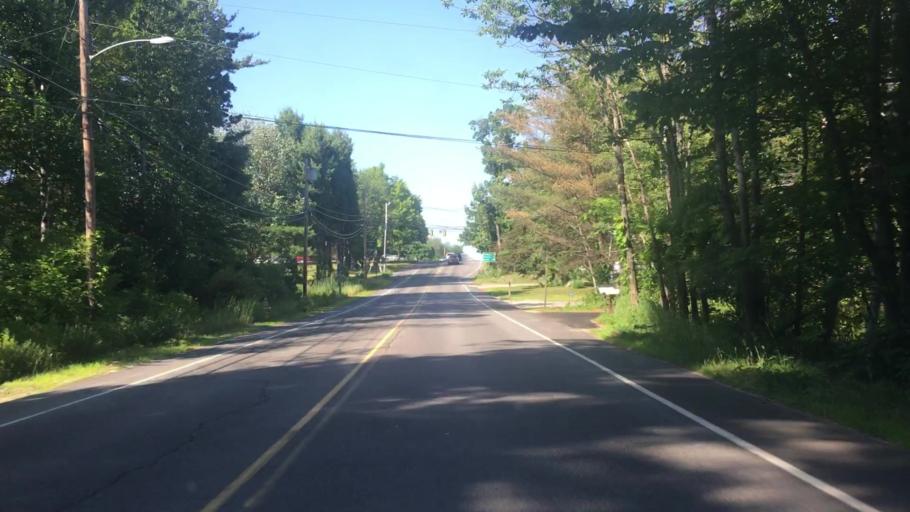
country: US
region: Maine
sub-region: York County
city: Buxton
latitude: 43.7342
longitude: -70.5523
